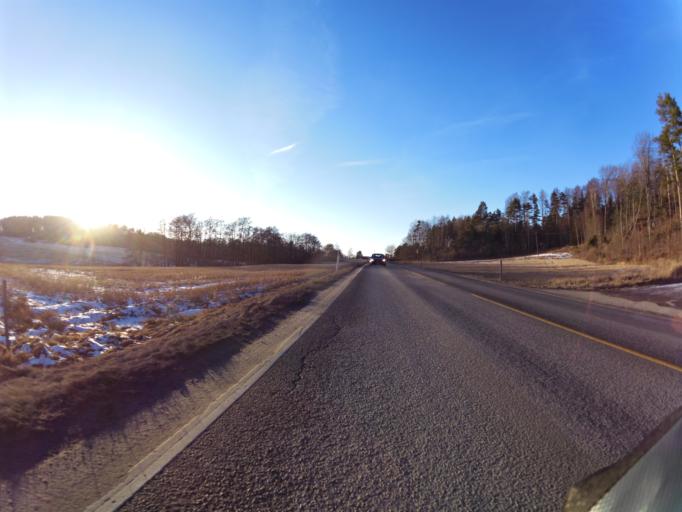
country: NO
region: Ostfold
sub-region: Fredrikstad
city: Fredrikstad
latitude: 59.2521
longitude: 10.8521
